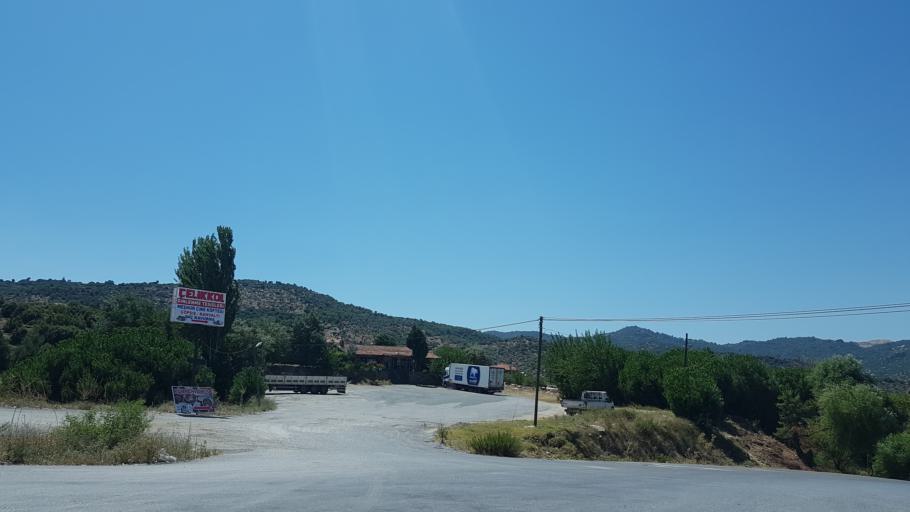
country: TR
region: Aydin
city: Akcaova
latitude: 37.4922
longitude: 28.1184
